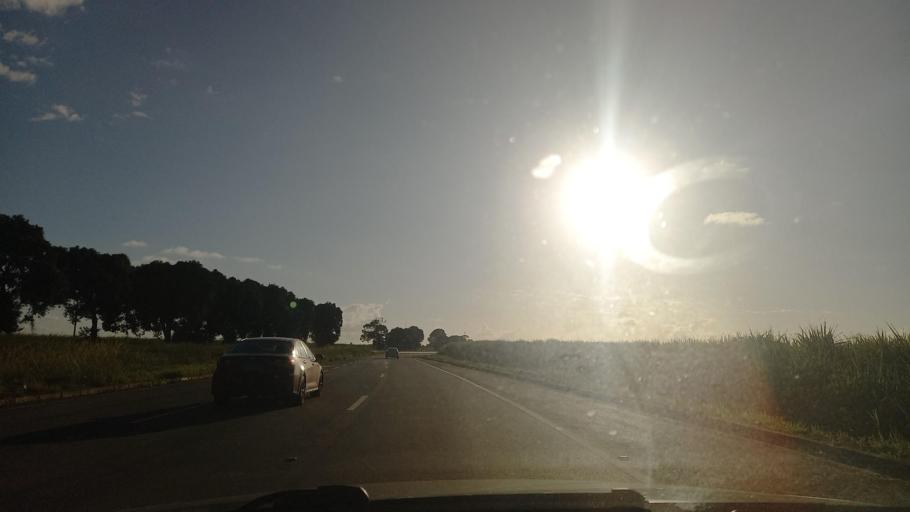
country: BR
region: Alagoas
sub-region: Campo Alegre
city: Campo Alegre
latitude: -9.7987
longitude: -36.2926
